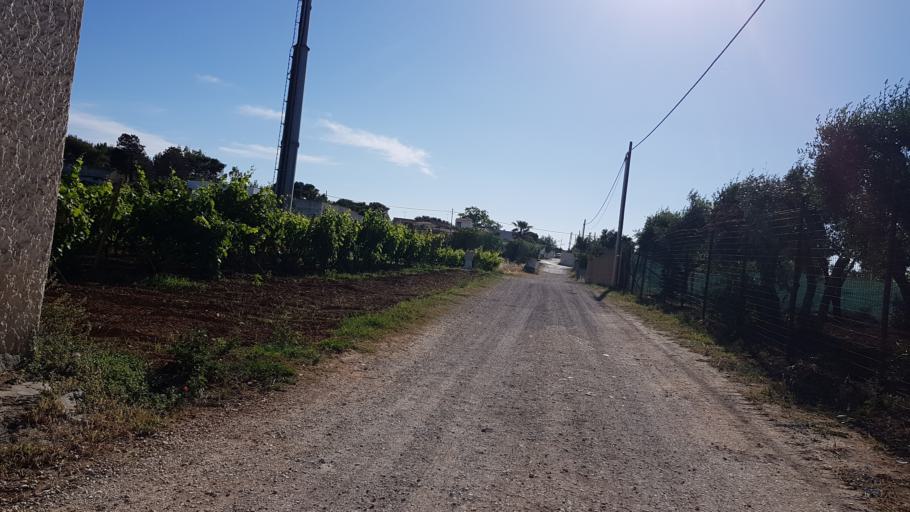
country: IT
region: Apulia
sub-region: Provincia di Brindisi
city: Brindisi
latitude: 40.6813
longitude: 17.8773
